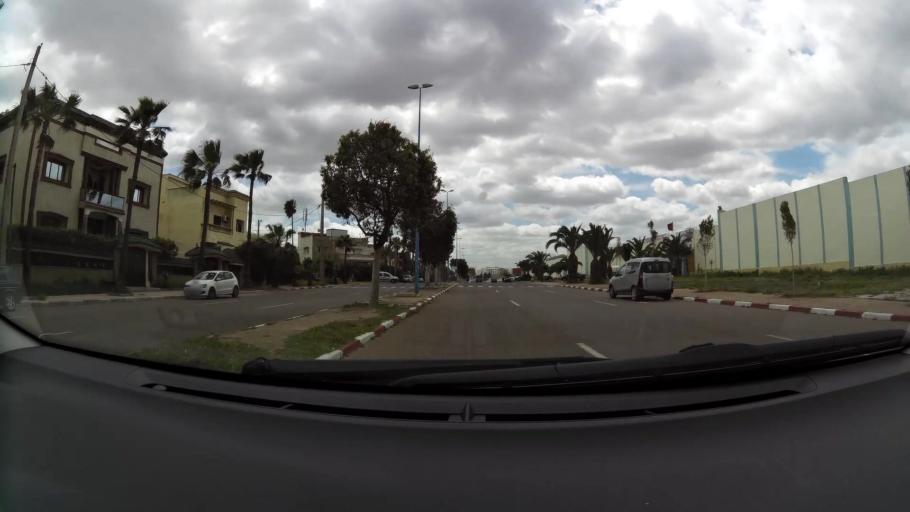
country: MA
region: Grand Casablanca
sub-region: Casablanca
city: Casablanca
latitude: 33.6116
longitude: -7.5500
